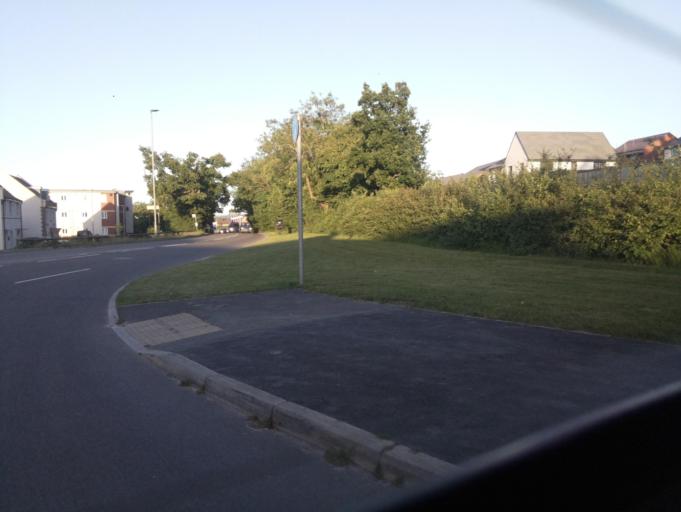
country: GB
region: England
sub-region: Devon
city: Newton Abbot
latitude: 50.5367
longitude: -3.6472
